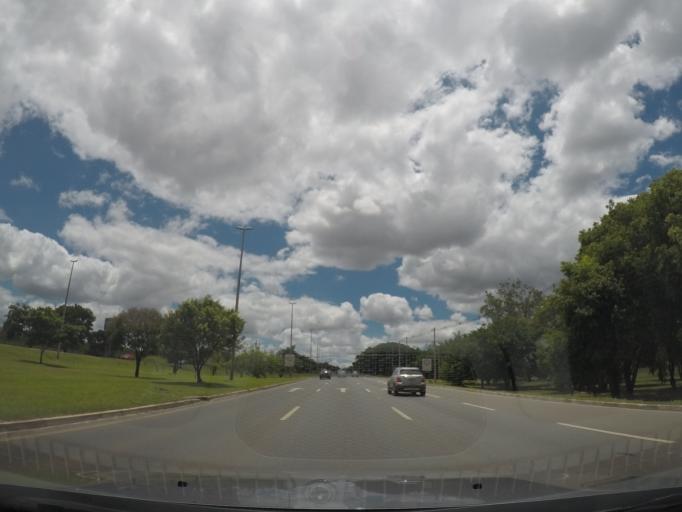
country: BR
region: Federal District
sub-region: Brasilia
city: Brasilia
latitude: -15.7391
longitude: -47.9165
